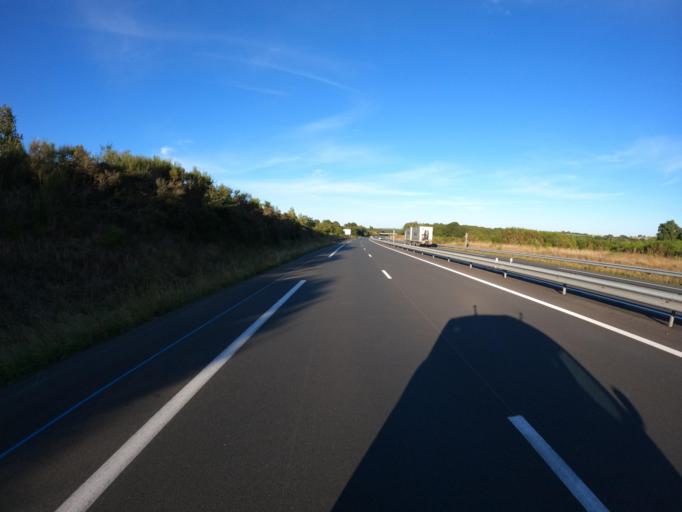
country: FR
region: Pays de la Loire
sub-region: Departement de la Vendee
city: Mortagne-sur-Sevre
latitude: 46.9548
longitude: -0.9401
